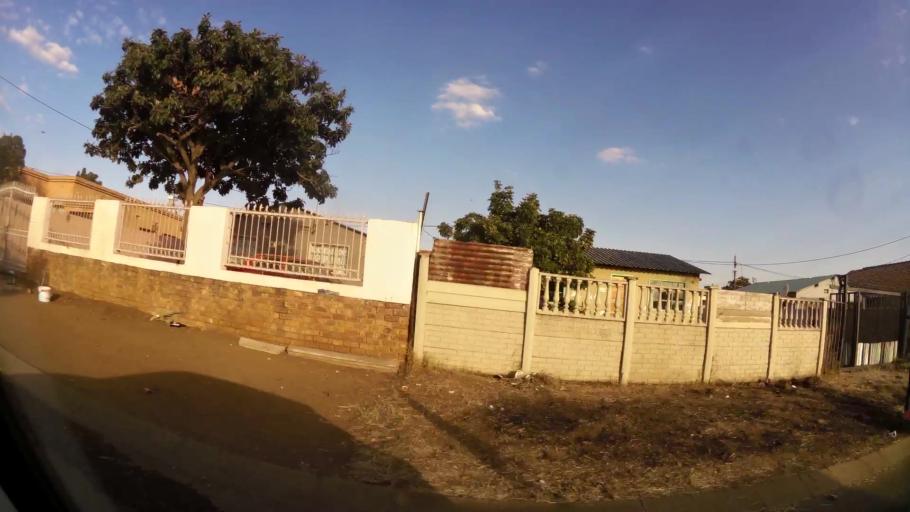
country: ZA
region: Gauteng
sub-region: City of Tshwane Metropolitan Municipality
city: Cullinan
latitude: -25.7131
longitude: 28.3722
